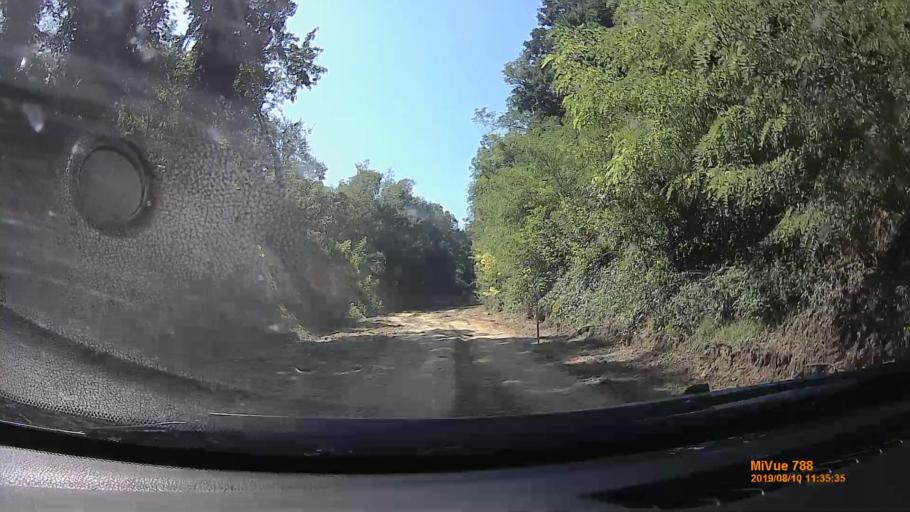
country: HU
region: Somogy
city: Somogyvar
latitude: 46.5158
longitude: 17.7768
